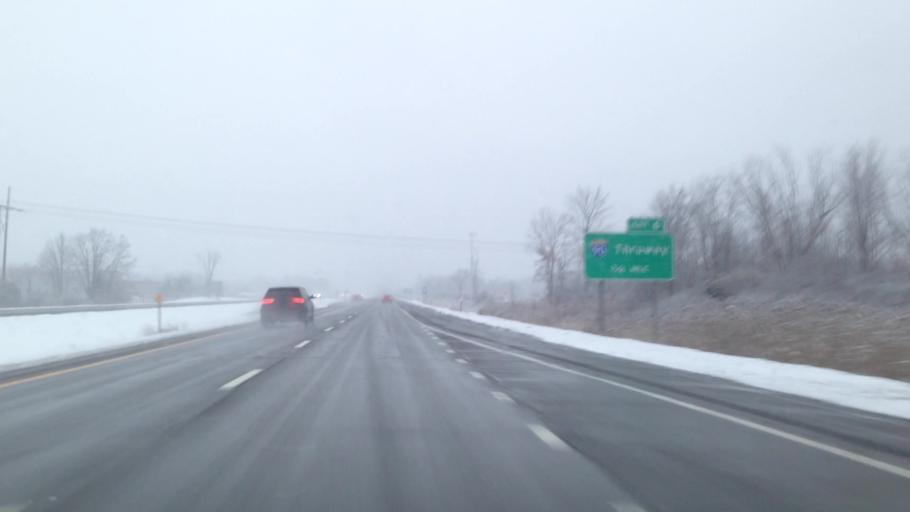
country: US
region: New York
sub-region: Onondaga County
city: East Syracuse
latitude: 43.0842
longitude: -76.0534
